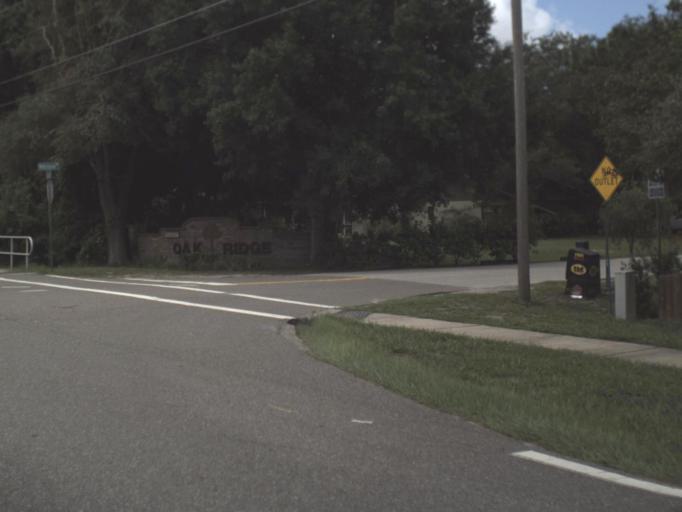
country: US
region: Florida
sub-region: Pasco County
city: Trinity
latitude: 28.1861
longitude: -82.6991
